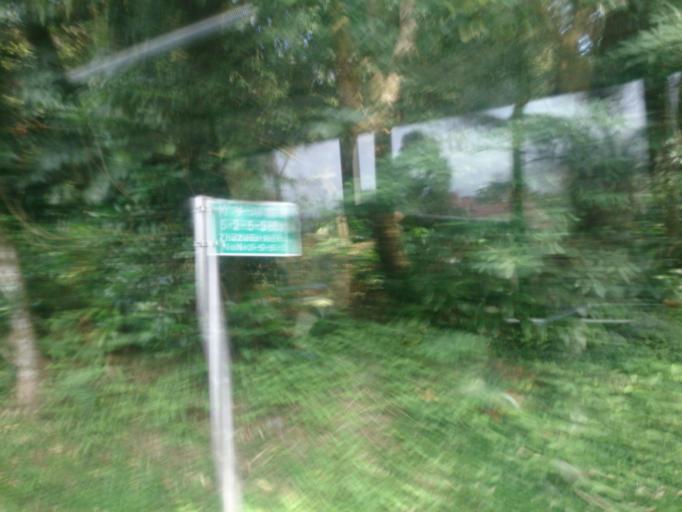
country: TW
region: Taipei
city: Taipei
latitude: 25.1612
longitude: 121.5444
